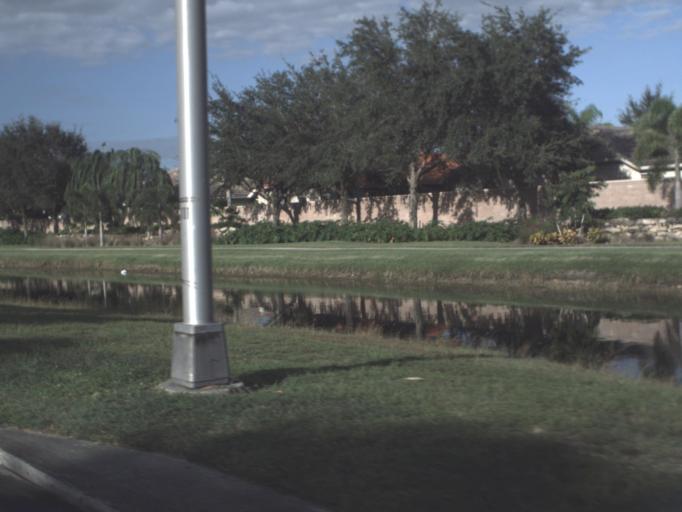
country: US
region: Florida
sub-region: Collier County
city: Pine Ridge
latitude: 26.2054
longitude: -81.7682
